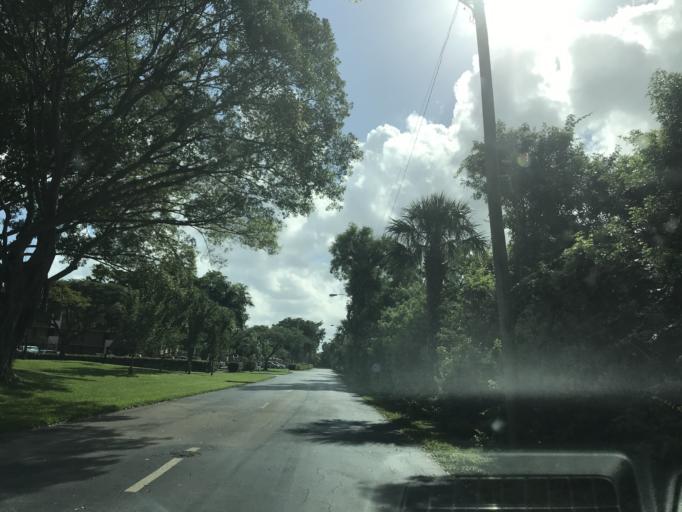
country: US
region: Florida
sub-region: Broward County
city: Margate
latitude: 26.2631
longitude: -80.1976
